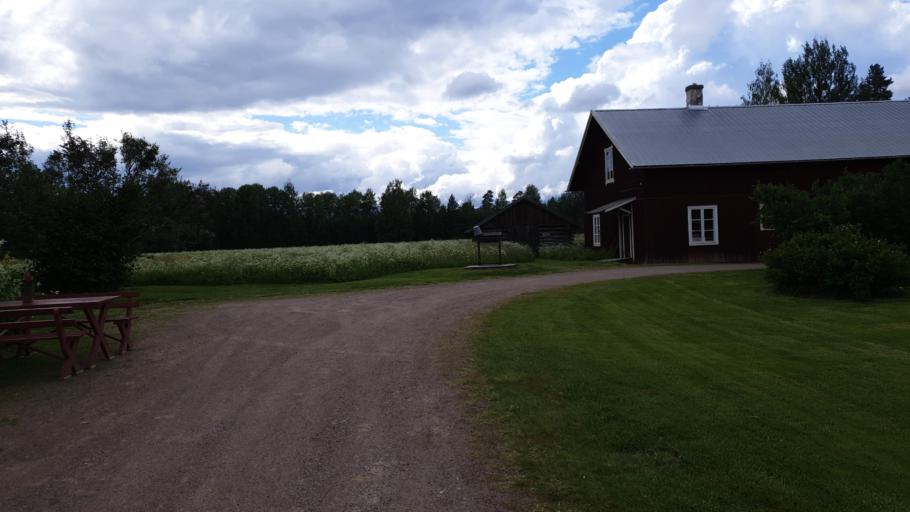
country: SE
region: Jaemtland
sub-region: Harjedalens Kommun
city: Sveg
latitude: 61.7961
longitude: 14.6348
